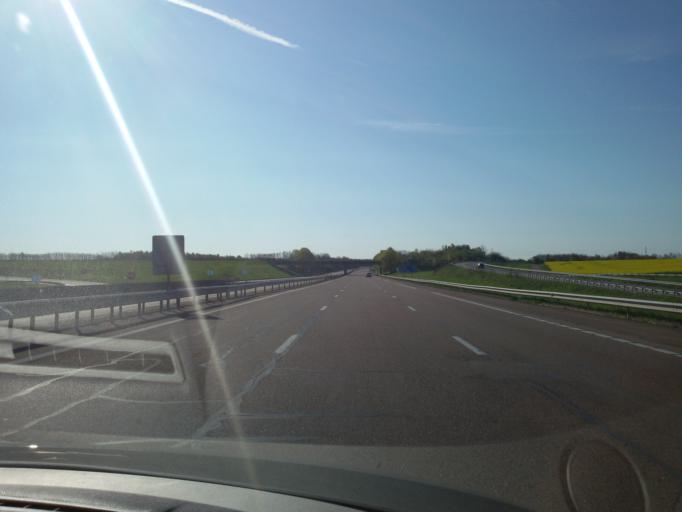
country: FR
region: Centre
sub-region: Departement du Loiret
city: Courtenay
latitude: 48.0533
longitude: 3.1017
